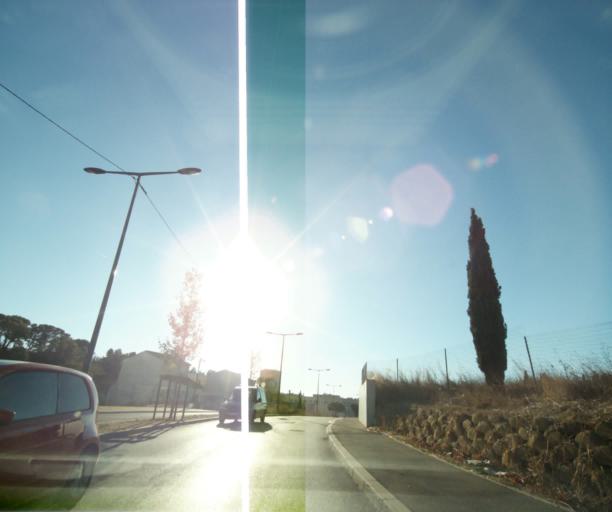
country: FR
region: Provence-Alpes-Cote d'Azur
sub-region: Departement des Bouches-du-Rhone
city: Plan-de-Cuques
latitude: 43.3397
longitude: 5.4414
